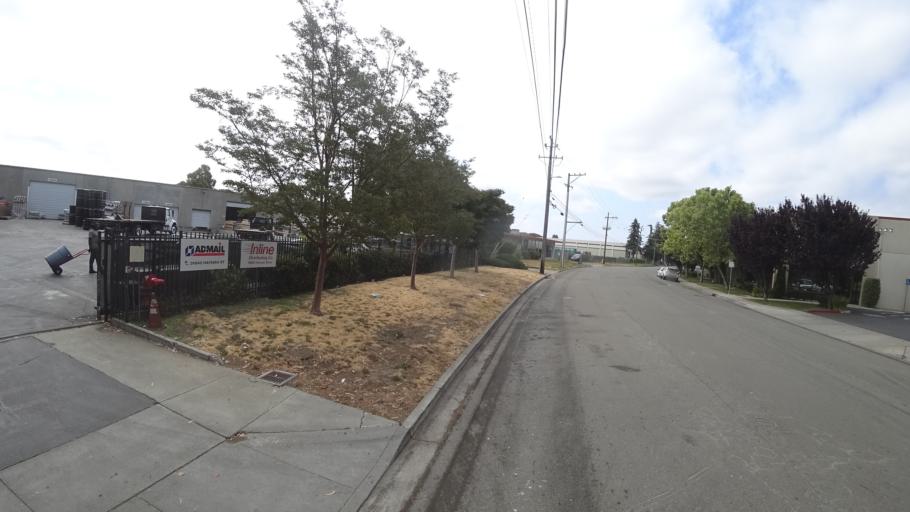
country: US
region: California
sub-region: Alameda County
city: Union City
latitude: 37.6126
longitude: -122.0451
